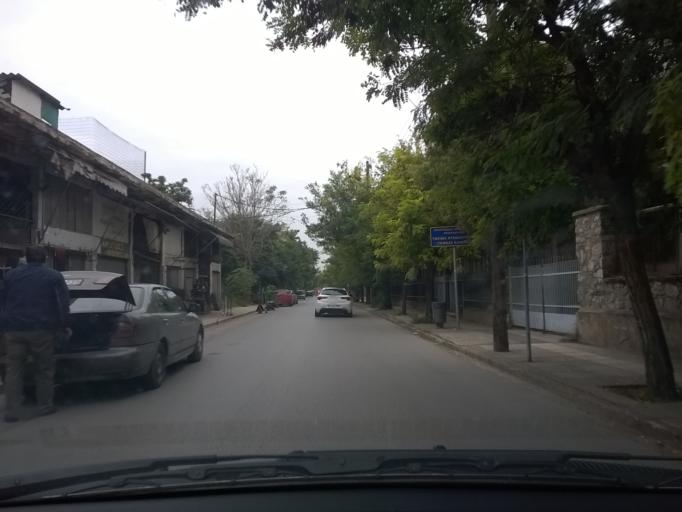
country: GR
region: Central Macedonia
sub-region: Nomos Thessalonikis
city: Thessaloniki
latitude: 40.6439
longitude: 22.9261
